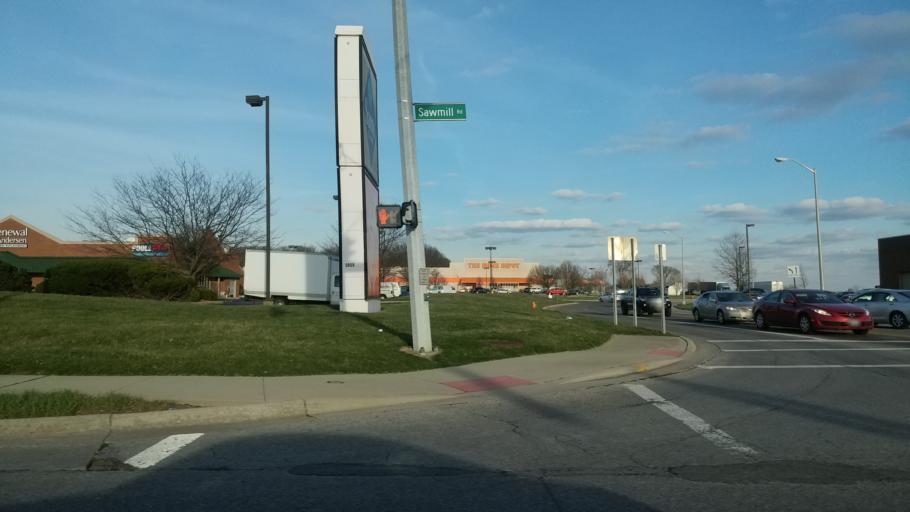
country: US
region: Ohio
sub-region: Franklin County
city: Dublin
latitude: 40.0852
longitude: -83.0920
